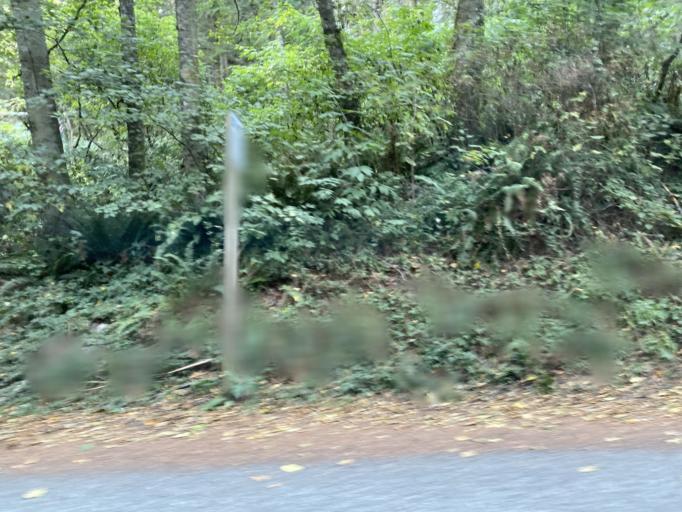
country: US
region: Washington
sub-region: Island County
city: Ault Field
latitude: 48.4193
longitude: -122.6609
